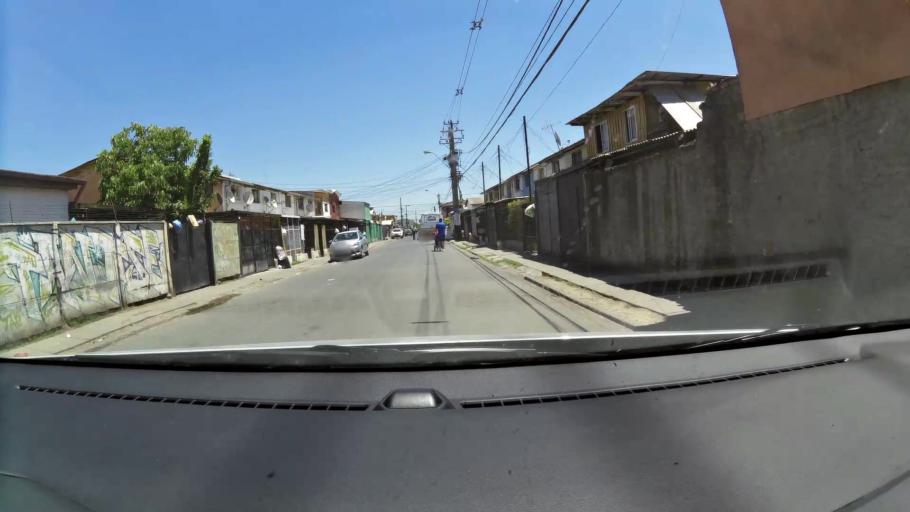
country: CL
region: Santiago Metropolitan
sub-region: Provincia de Maipo
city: San Bernardo
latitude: -33.5820
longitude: -70.6712
